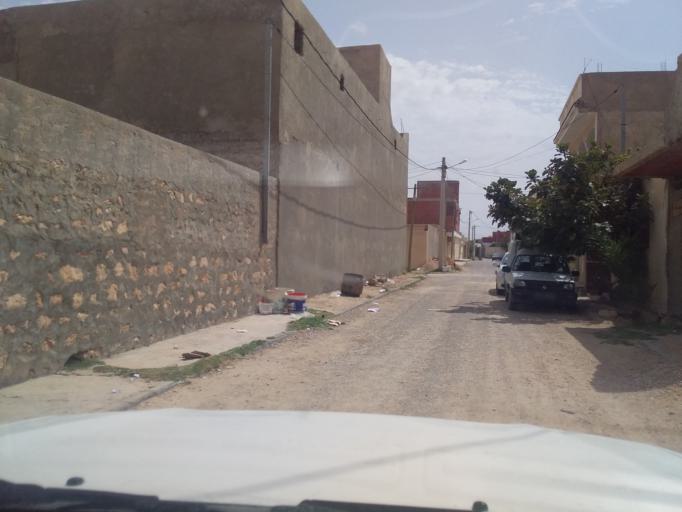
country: TN
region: Qabis
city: Matmata
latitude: 33.6208
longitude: 10.2743
